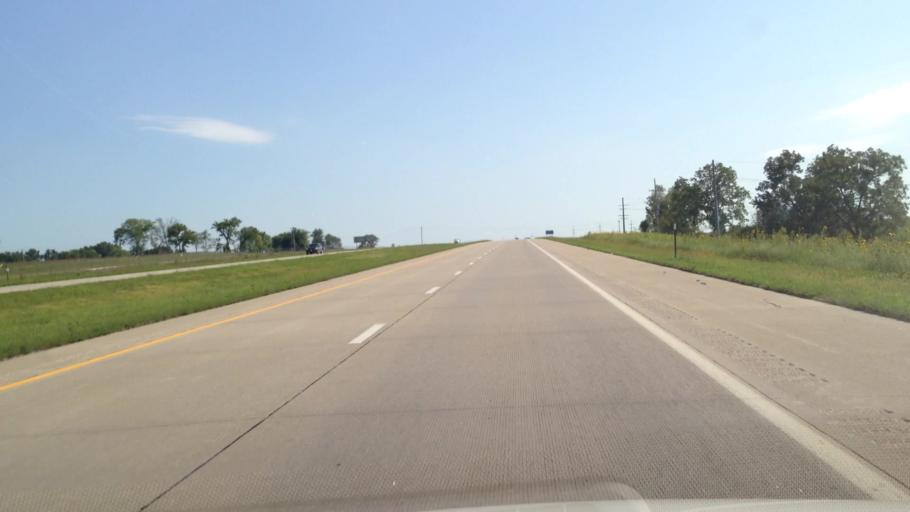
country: US
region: Kansas
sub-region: Linn County
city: Pleasanton
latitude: 38.2003
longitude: -94.7056
